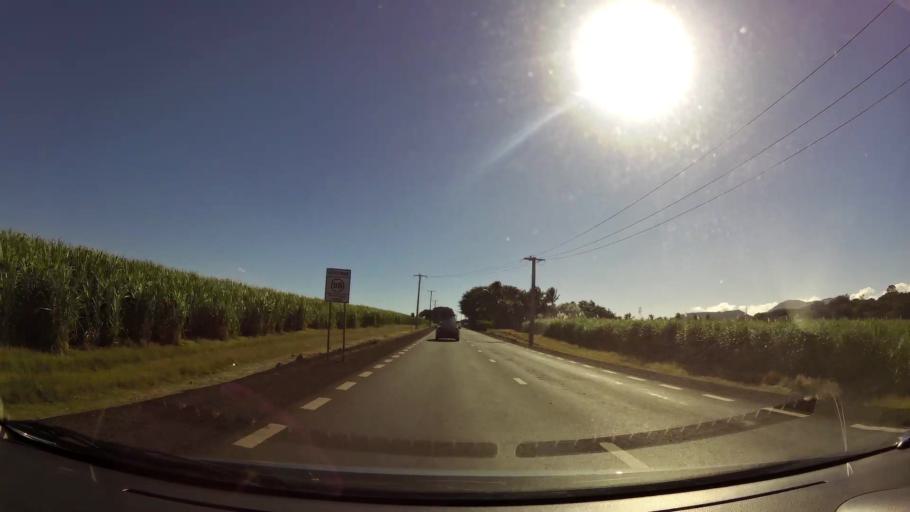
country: MU
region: Black River
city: Cascavelle
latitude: -20.2929
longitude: 57.4019
